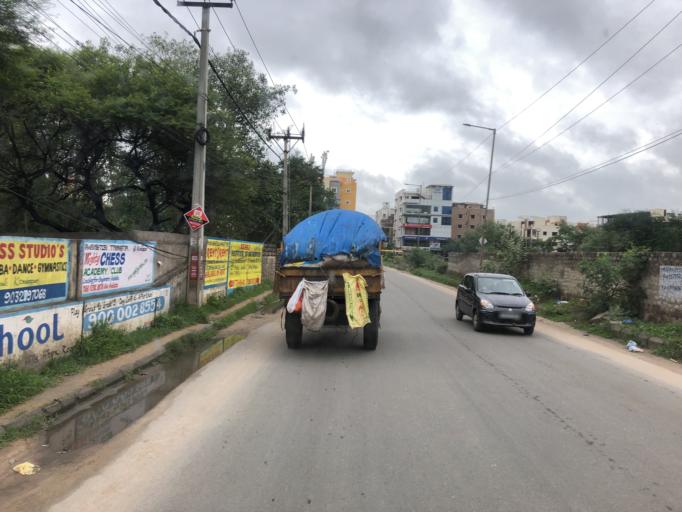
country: IN
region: Telangana
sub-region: Rangareddi
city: Kukatpalli
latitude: 17.4648
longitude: 78.3706
